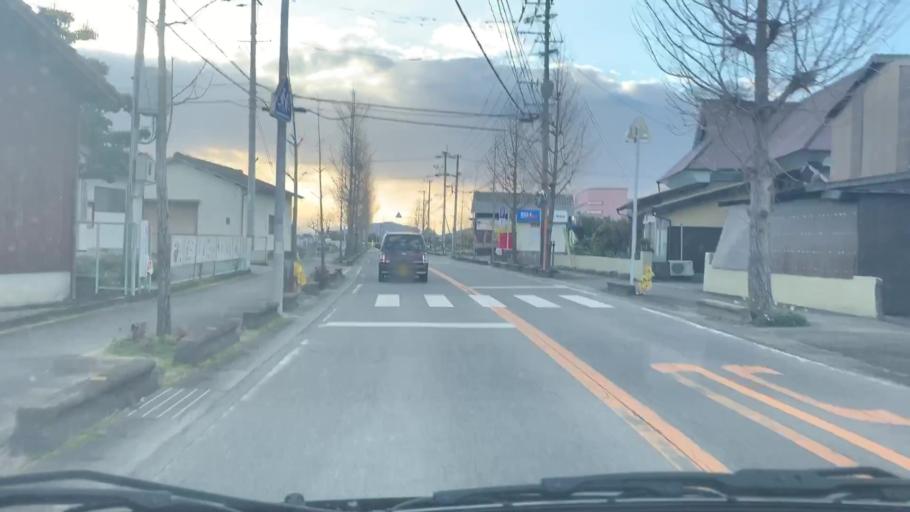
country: JP
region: Saga Prefecture
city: Saga-shi
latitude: 33.2550
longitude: 130.2587
